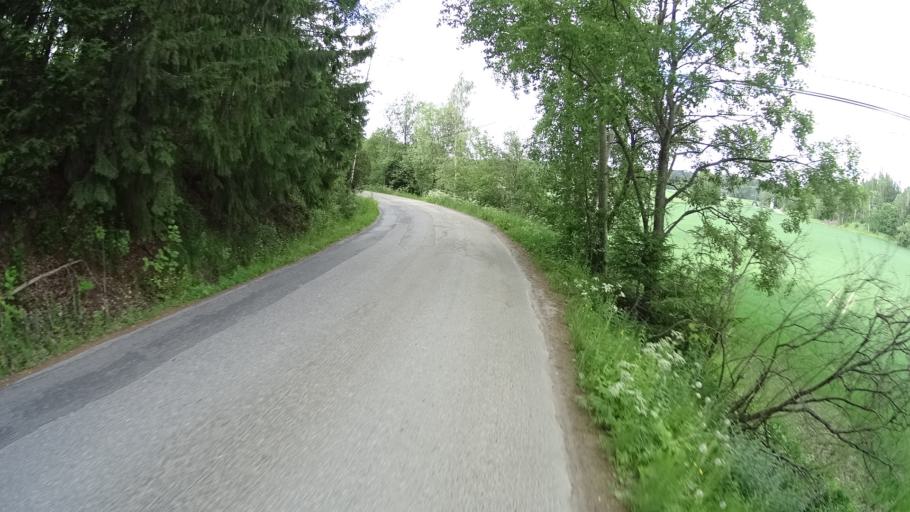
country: FI
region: Uusimaa
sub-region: Helsinki
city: Sibbo
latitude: 60.2895
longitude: 25.3102
